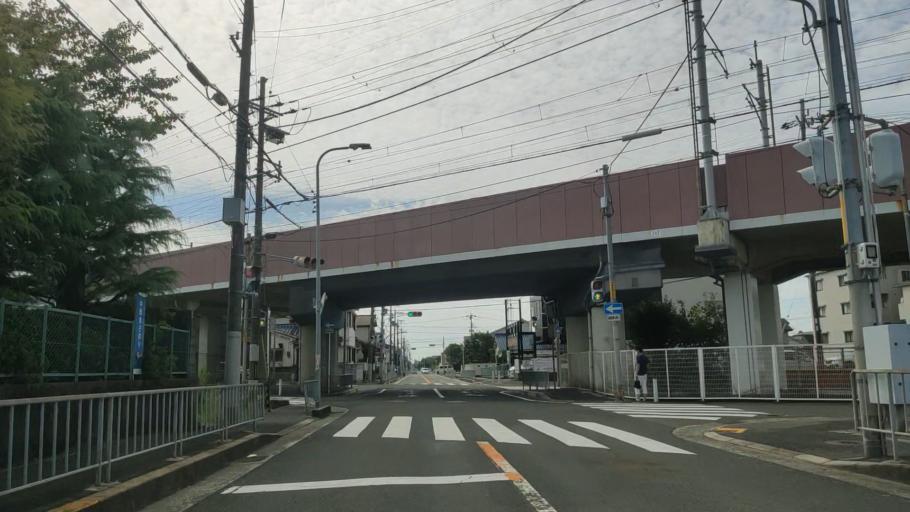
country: JP
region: Osaka
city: Ikeda
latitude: 34.8154
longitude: 135.4351
